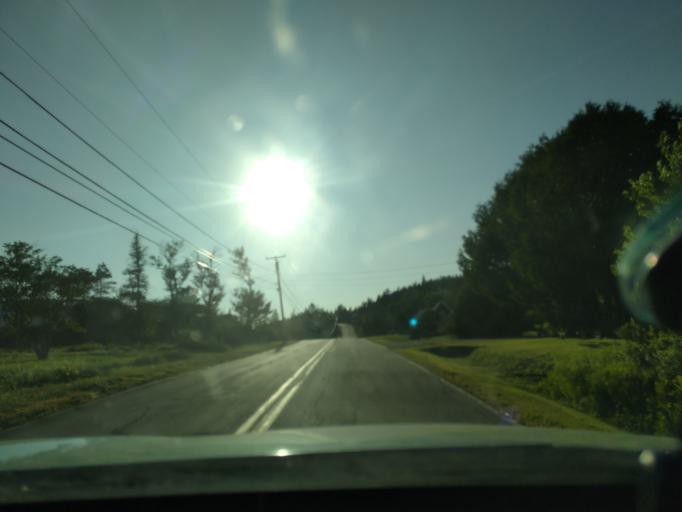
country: US
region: Maine
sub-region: Washington County
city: Machiasport
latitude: 44.6586
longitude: -67.2138
